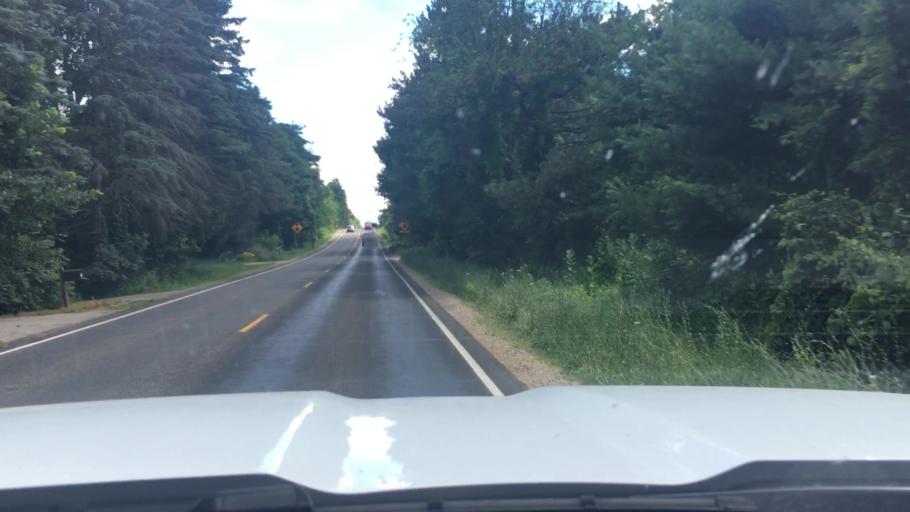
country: US
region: Michigan
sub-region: Kent County
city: Rockford
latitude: 43.1634
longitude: -85.6111
